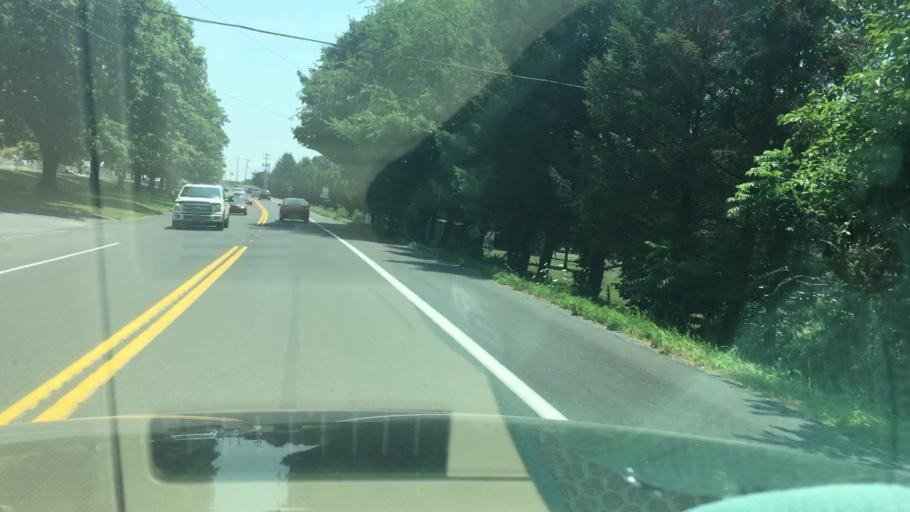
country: US
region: Pennsylvania
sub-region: Lehigh County
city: Schnecksville
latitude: 40.6803
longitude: -75.7262
